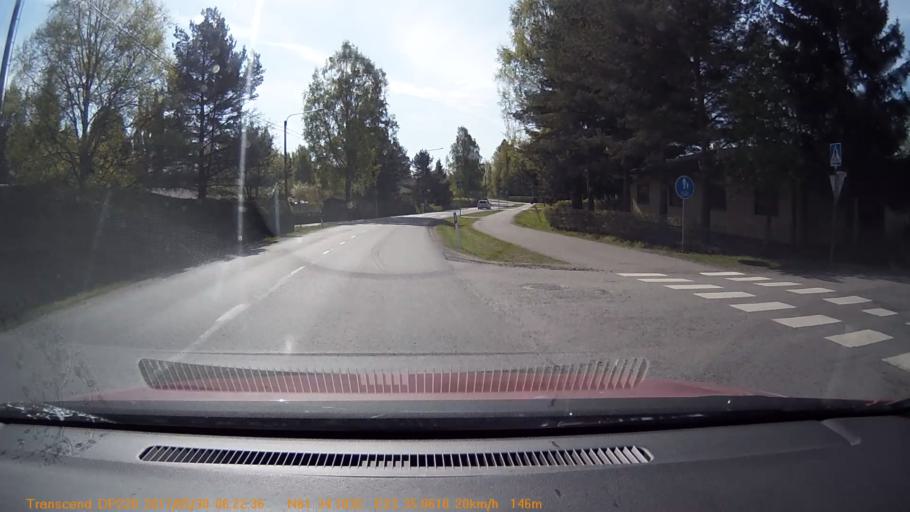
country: FI
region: Pirkanmaa
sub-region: Tampere
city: Yloejaervi
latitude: 61.5698
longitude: 23.5843
